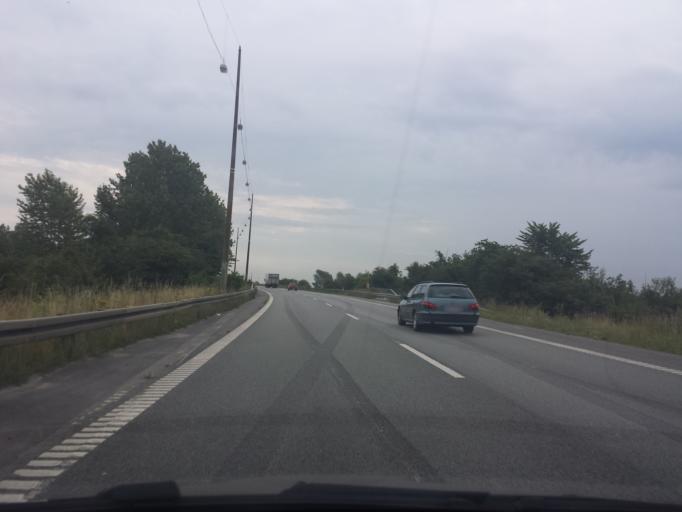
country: DK
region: Capital Region
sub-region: Ishoj Kommune
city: Ishoj
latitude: 55.6419
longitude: 12.3379
